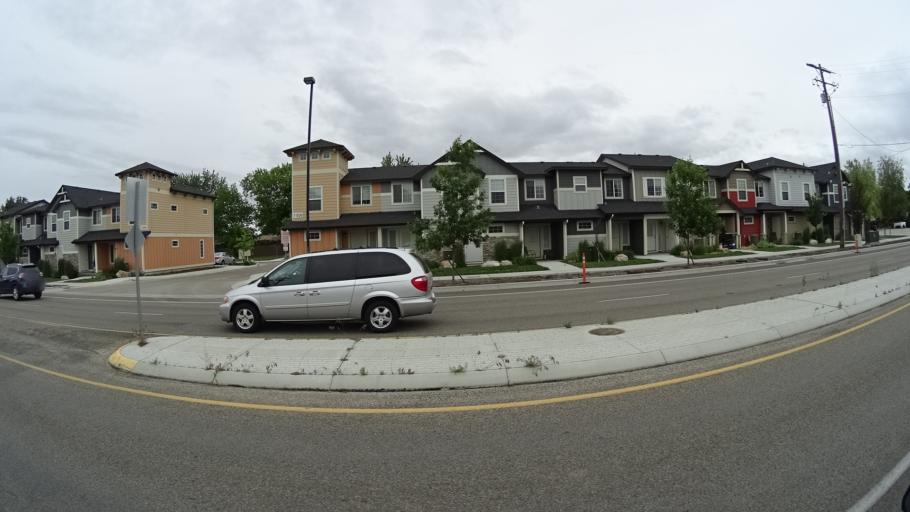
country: US
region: Idaho
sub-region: Ada County
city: Eagle
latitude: 43.6338
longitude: -116.3197
